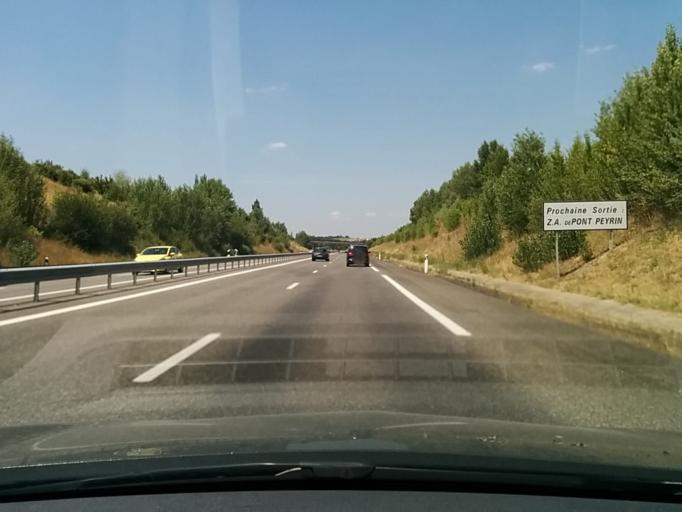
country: FR
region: Midi-Pyrenees
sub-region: Departement du Gers
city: Pujaudran
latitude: 43.6028
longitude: 1.0827
